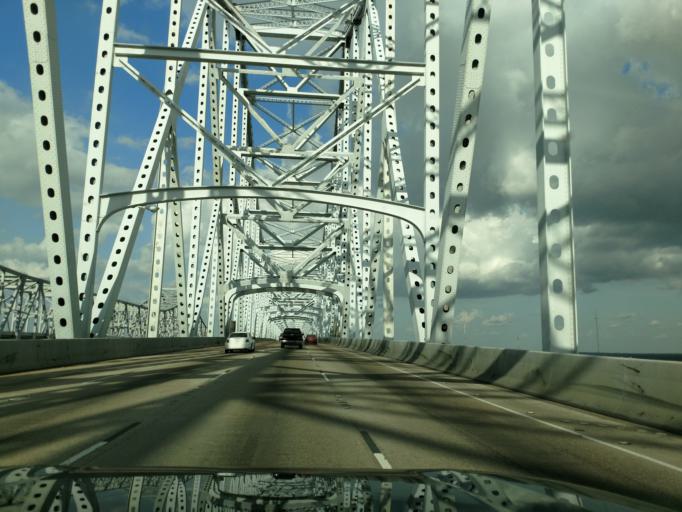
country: US
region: Louisiana
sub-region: Orleans Parish
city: New Orleans
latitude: 29.9376
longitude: -90.0600
